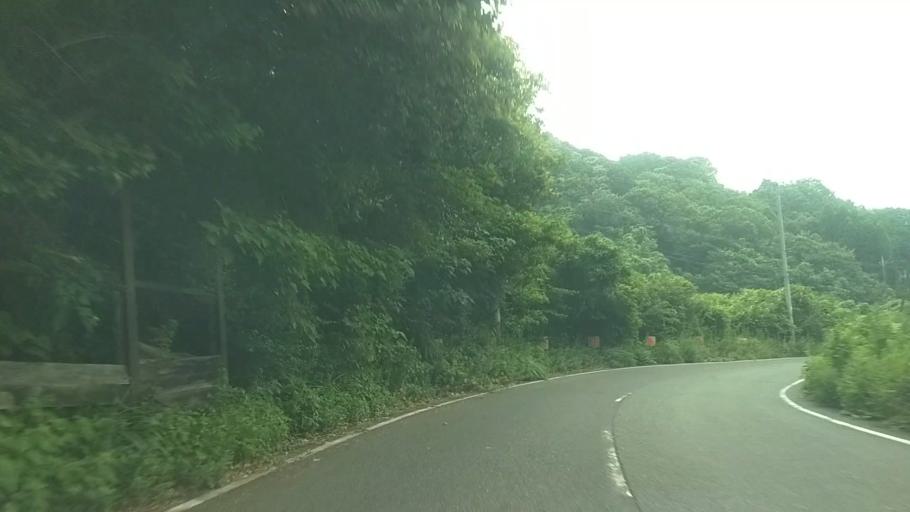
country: JP
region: Chiba
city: Kimitsu
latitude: 35.2402
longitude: 139.9825
